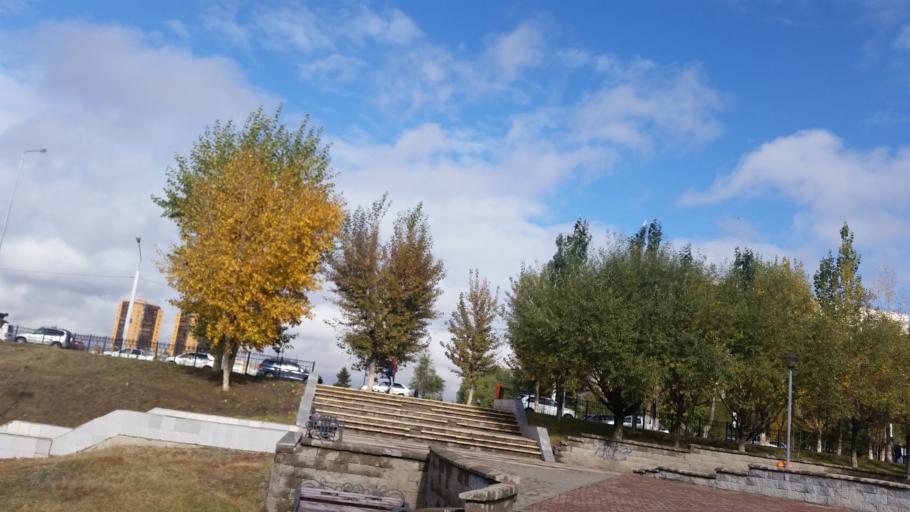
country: KZ
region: Astana Qalasy
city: Astana
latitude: 51.1599
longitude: 71.4699
